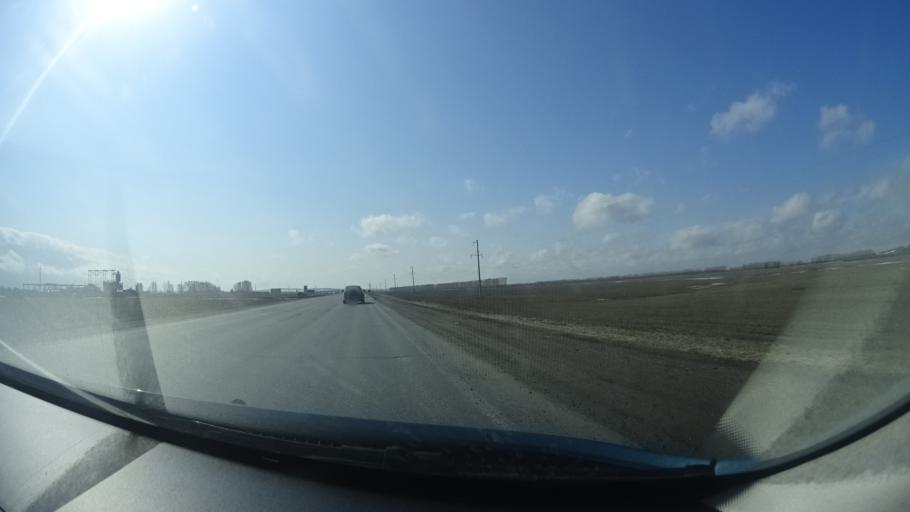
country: RU
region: Bashkortostan
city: Mikhaylovka
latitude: 54.9572
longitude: 55.7576
